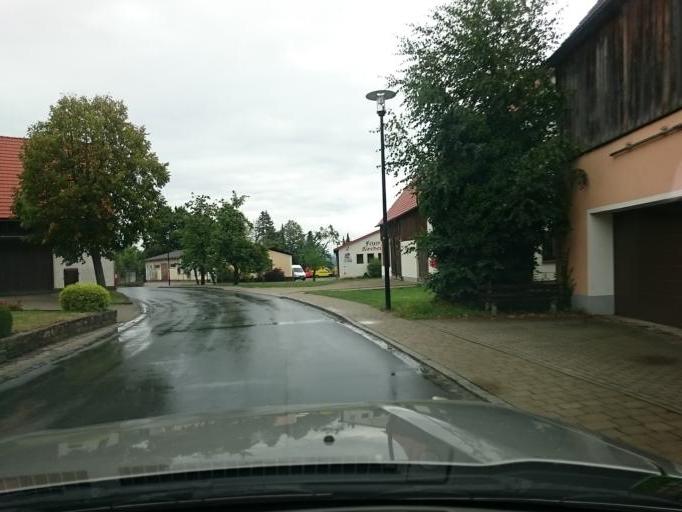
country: DE
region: Bavaria
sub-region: Upper Franconia
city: Pottenstein
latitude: 49.7437
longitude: 11.4014
